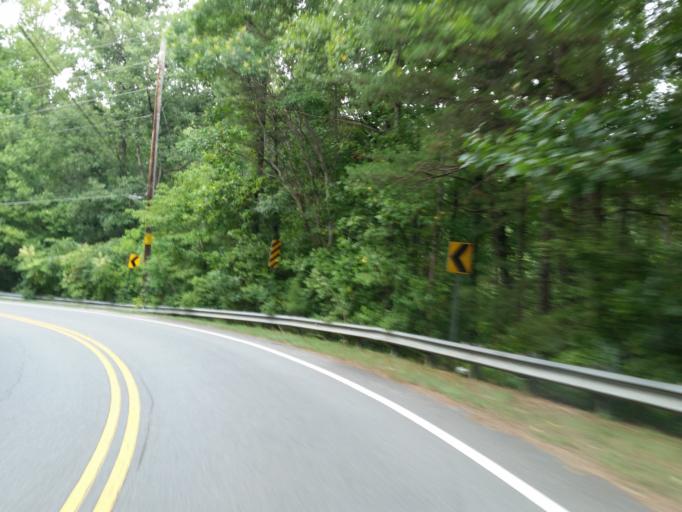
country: US
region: Georgia
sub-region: Fulton County
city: Roswell
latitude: 34.0462
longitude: -84.4329
